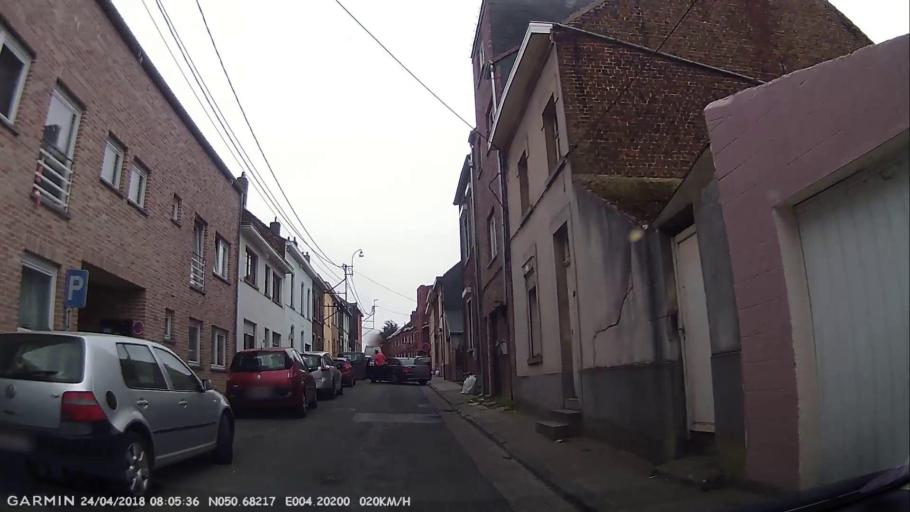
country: BE
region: Wallonia
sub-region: Province du Brabant Wallon
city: Tubize
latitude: 50.6822
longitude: 4.2020
